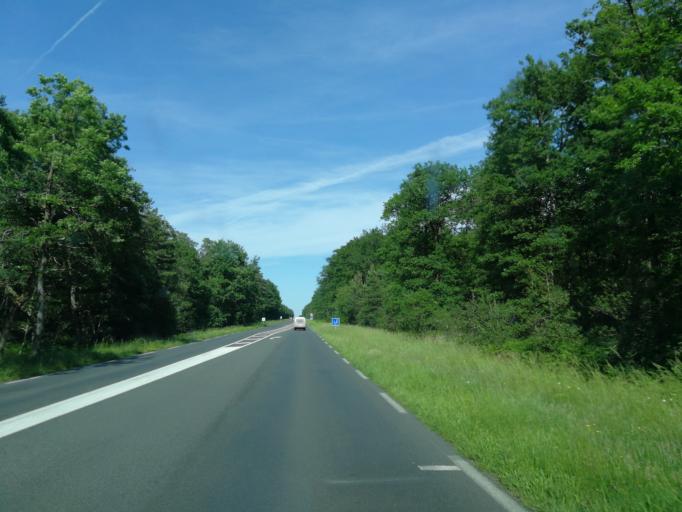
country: FR
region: Centre
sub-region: Departement d'Indre-et-Loire
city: Cheille
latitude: 47.2148
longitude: 0.3587
